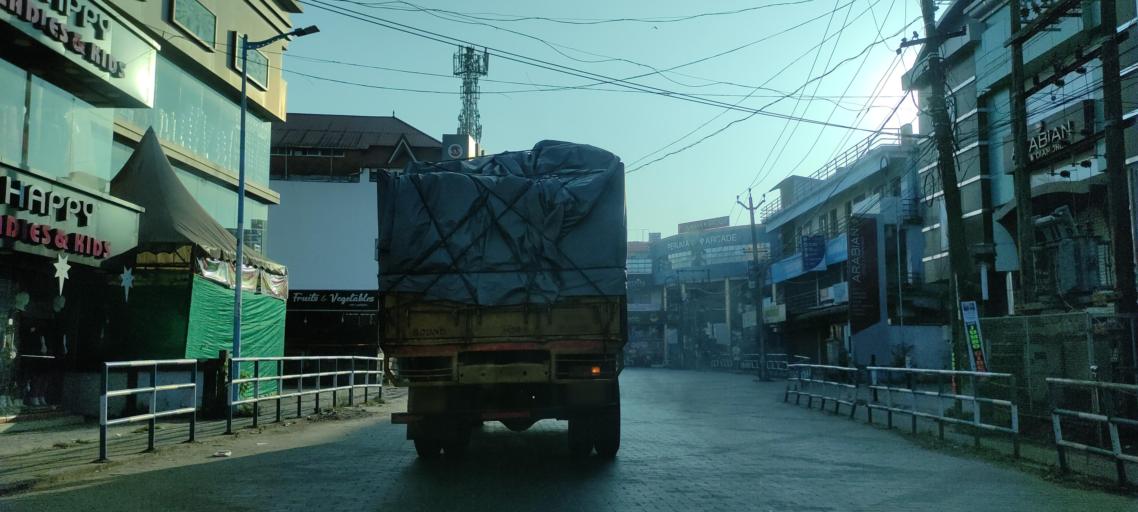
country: IN
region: Kerala
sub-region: Alappuzha
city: Kayankulam
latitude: 9.1745
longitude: 76.5001
